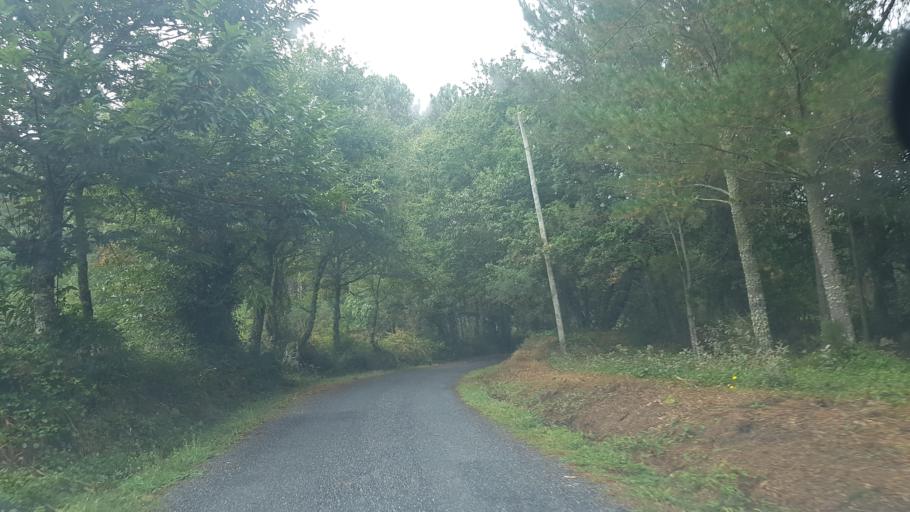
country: ES
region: Galicia
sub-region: Provincia de Lugo
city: Friol
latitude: 43.1259
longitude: -7.8152
